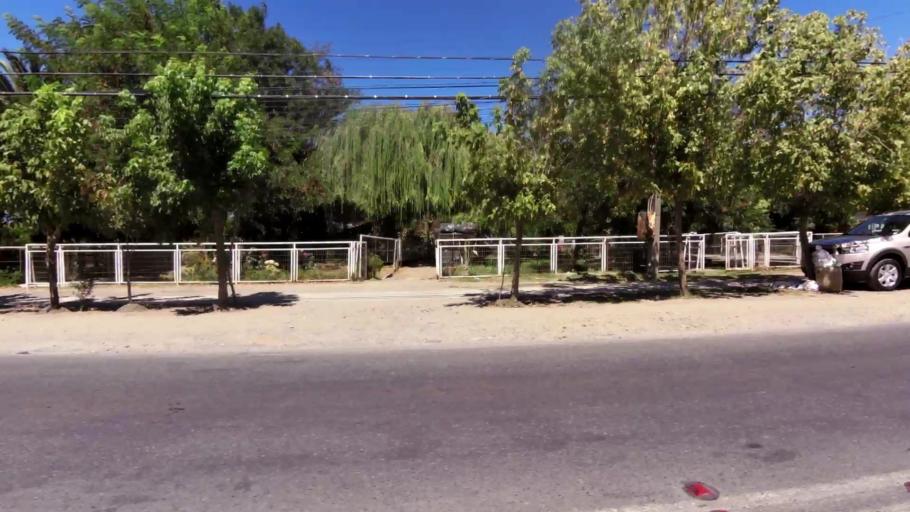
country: CL
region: O'Higgins
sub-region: Provincia de Cachapoal
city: Rancagua
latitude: -34.1679
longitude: -70.7739
